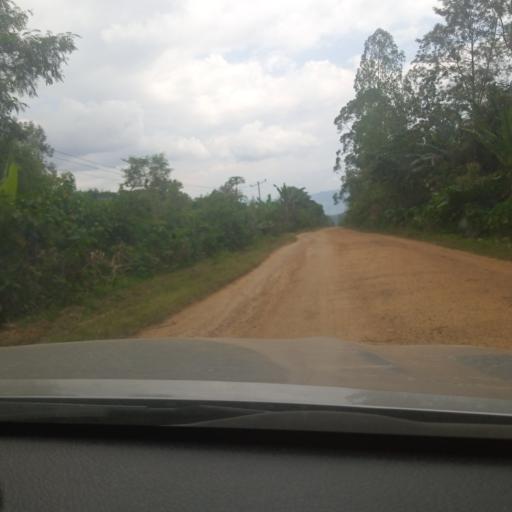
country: ET
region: Southern Nations, Nationalities, and People's Region
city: Tippi
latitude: 7.1421
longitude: 35.4181
